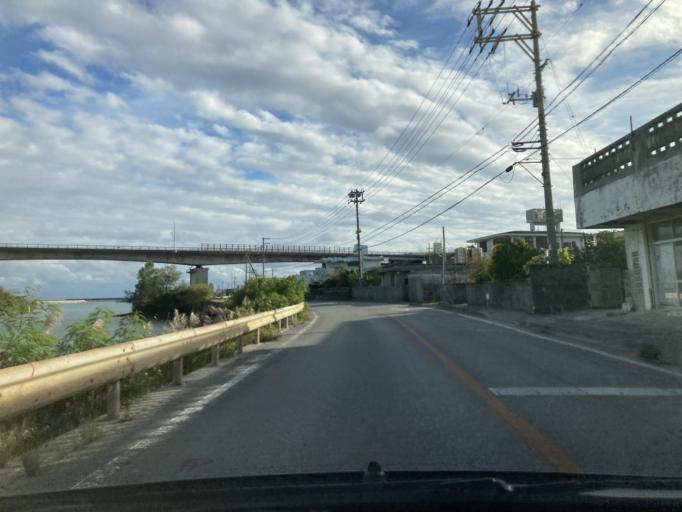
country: JP
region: Okinawa
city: Itoman
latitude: 26.1309
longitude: 127.7596
